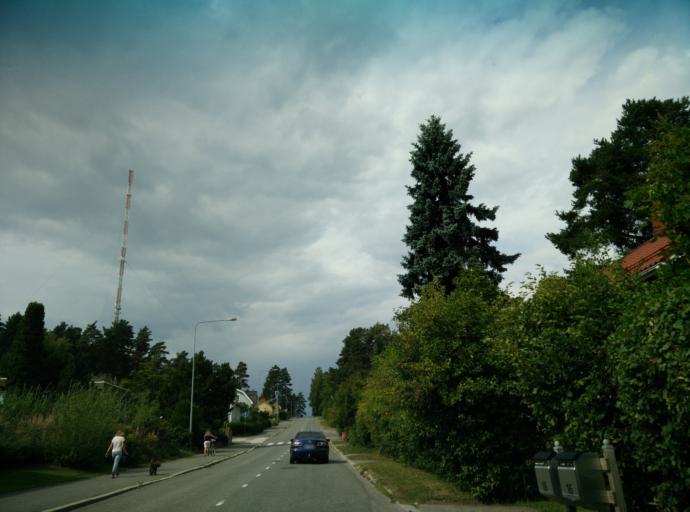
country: FI
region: Haeme
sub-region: Haemeenlinna
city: Haemeenlinna
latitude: 60.9863
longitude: 24.4539
